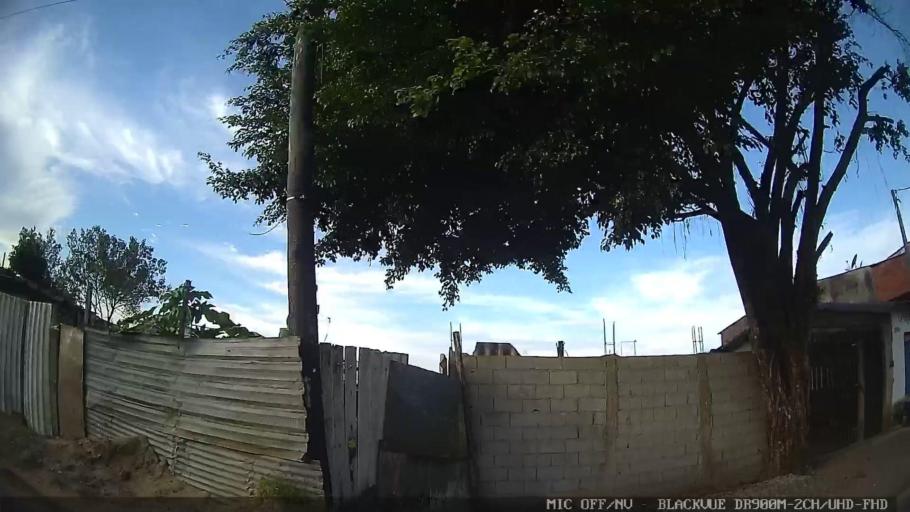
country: BR
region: Sao Paulo
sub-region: Itanhaem
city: Itanhaem
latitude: -24.1573
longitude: -46.7835
